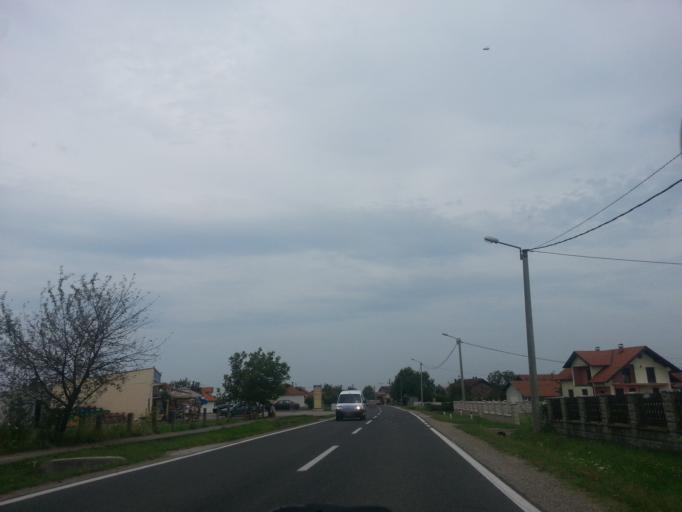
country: BA
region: Brcko
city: Brcko
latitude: 44.8230
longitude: 18.8160
